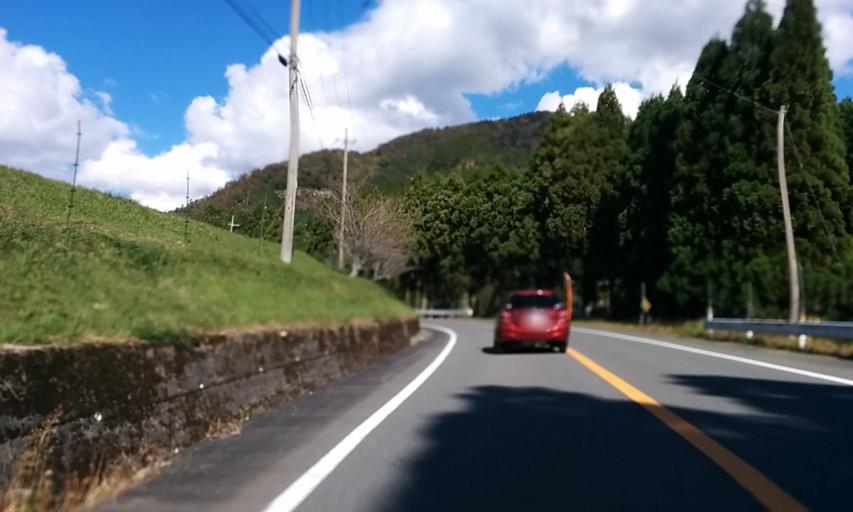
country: JP
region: Kyoto
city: Maizuru
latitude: 35.2908
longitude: 135.5575
